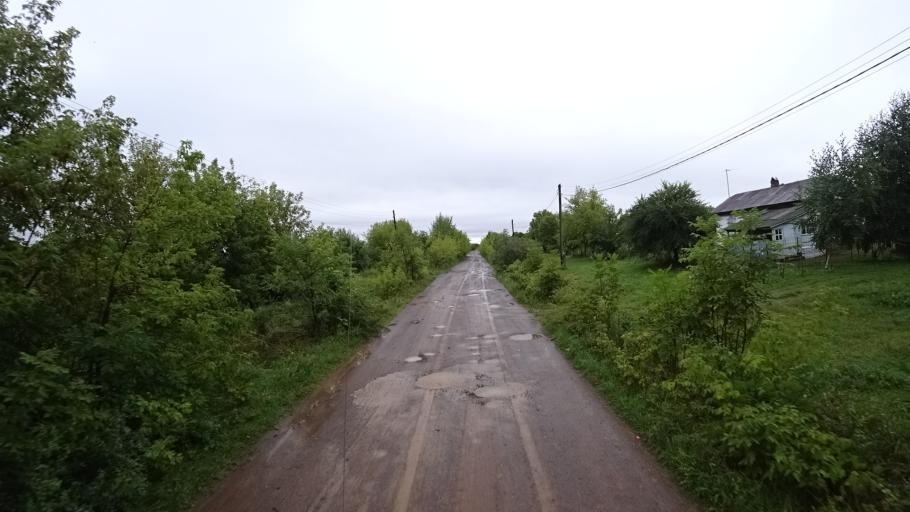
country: RU
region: Primorskiy
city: Monastyrishche
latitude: 44.2601
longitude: 132.4241
